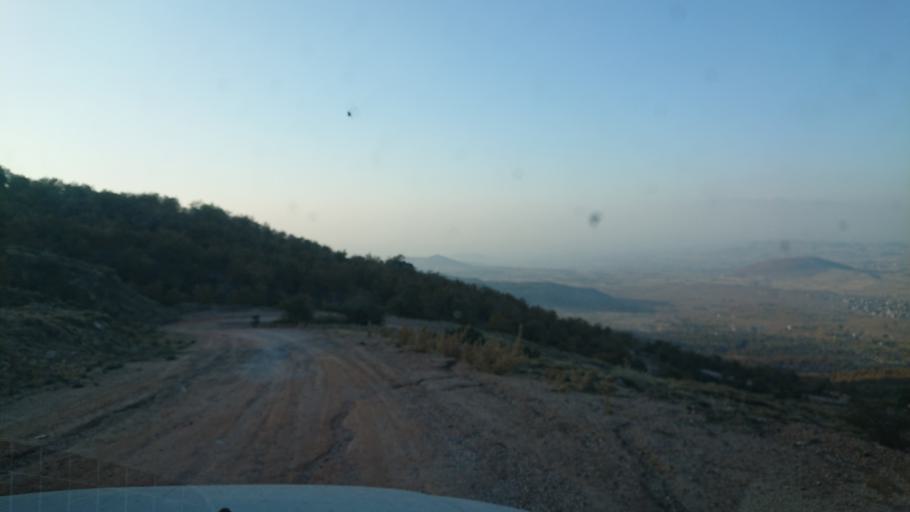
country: TR
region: Aksaray
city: Taspinar
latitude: 38.1691
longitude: 34.1811
